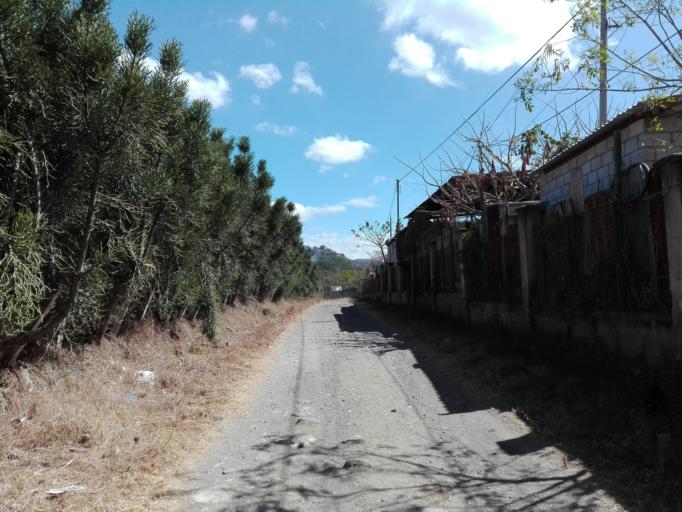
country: GT
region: Guatemala
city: Amatitlan
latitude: 14.4766
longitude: -90.5966
